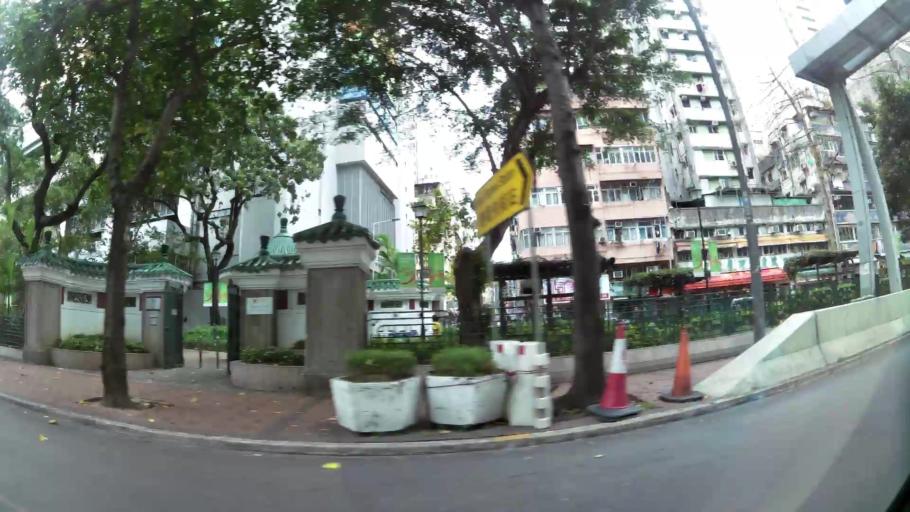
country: HK
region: Kowloon City
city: Kowloon
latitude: 22.3040
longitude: 114.1684
